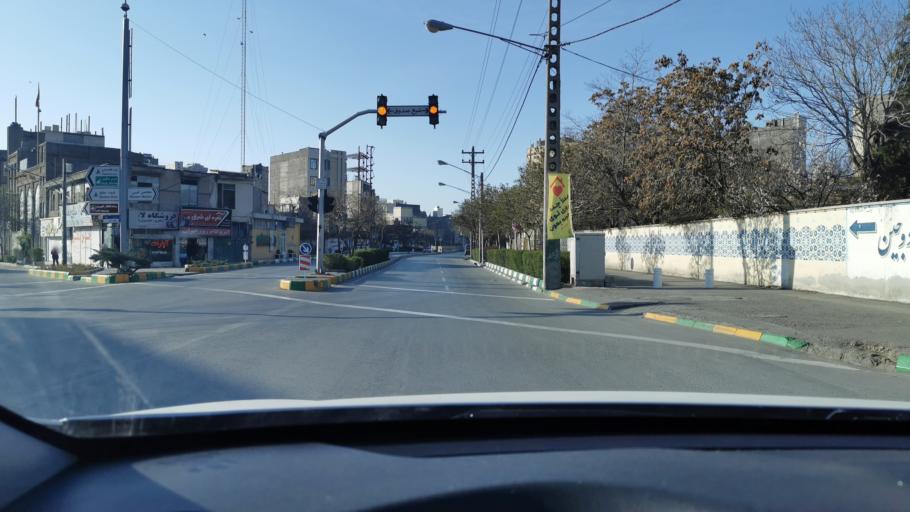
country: IR
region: Razavi Khorasan
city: Mashhad
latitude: 36.3057
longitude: 59.6341
